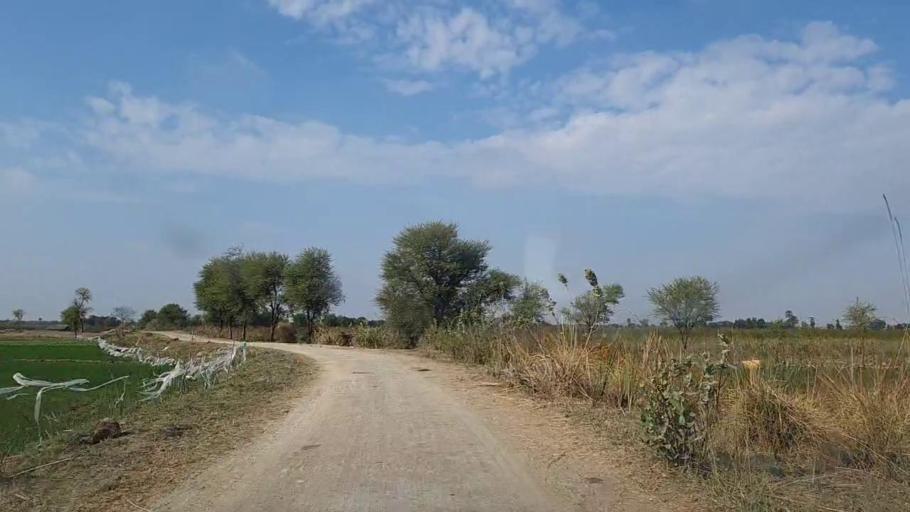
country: PK
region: Sindh
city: Sanghar
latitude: 26.2536
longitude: 69.0112
